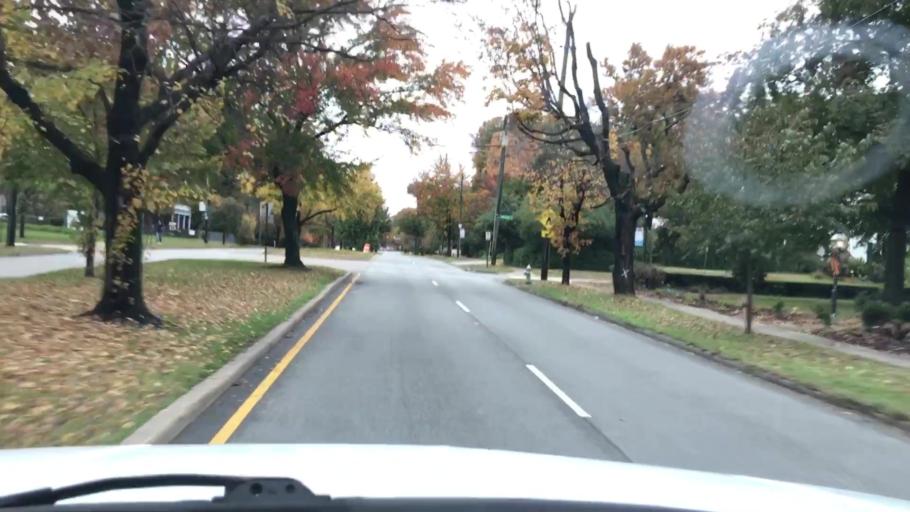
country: US
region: Virginia
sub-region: City of Richmond
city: Richmond
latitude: 37.5812
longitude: -77.4467
